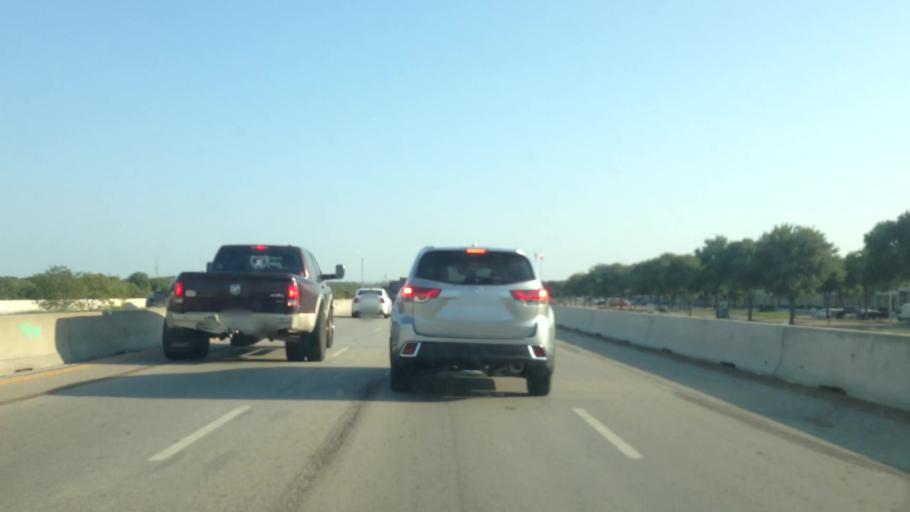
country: US
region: Texas
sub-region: Tarrant County
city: Richland Hills
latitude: 32.7936
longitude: -97.2121
